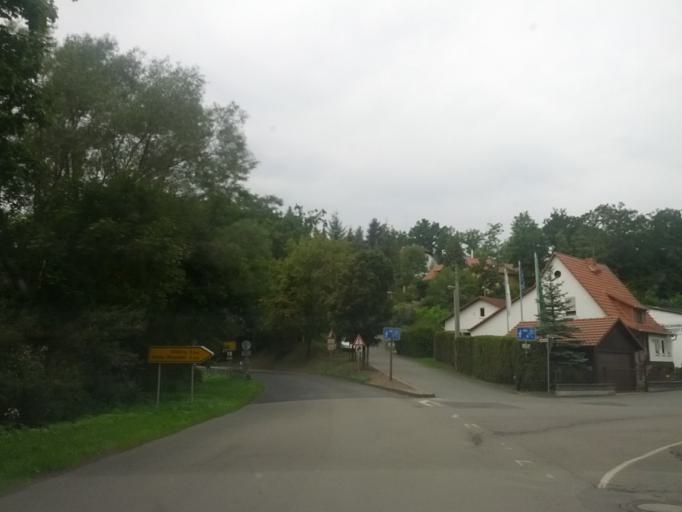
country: DE
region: Thuringia
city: Bad Salzungen
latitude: 50.8202
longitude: 10.2227
